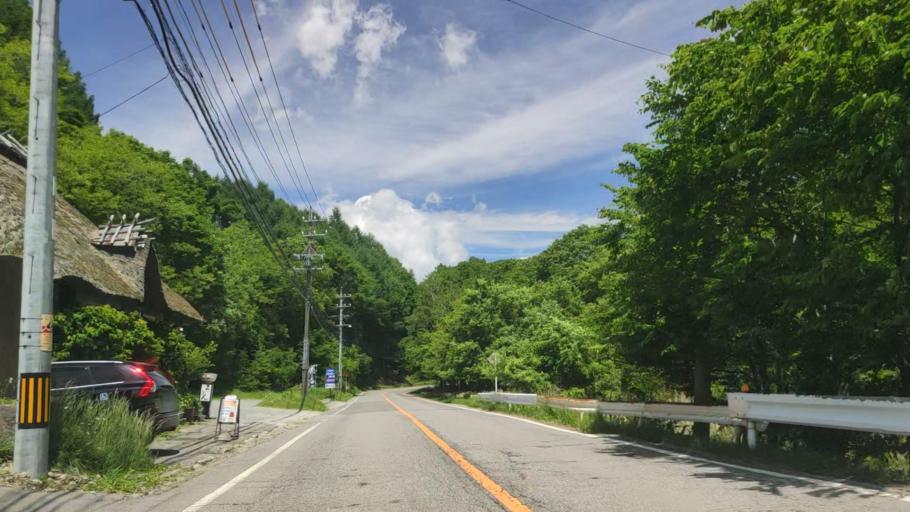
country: JP
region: Nagano
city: Suwa
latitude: 36.1256
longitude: 138.2303
